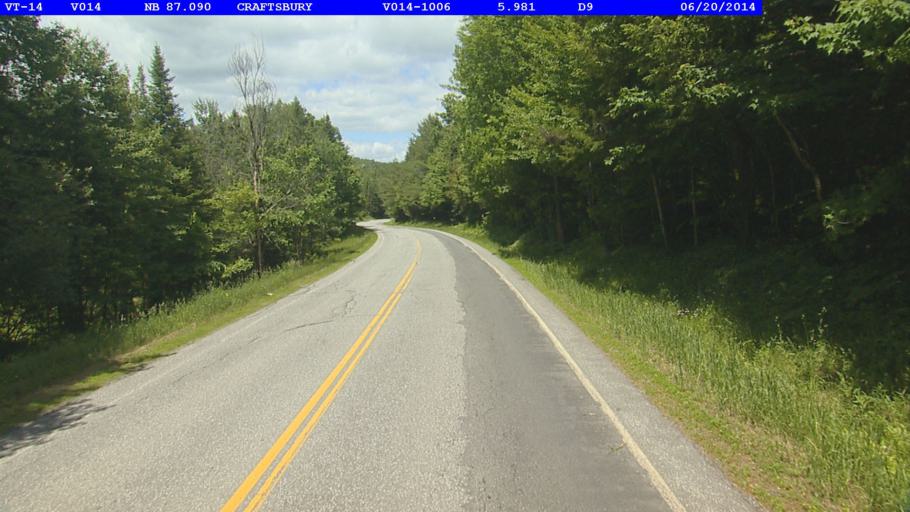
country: US
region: Vermont
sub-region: Caledonia County
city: Hardwick
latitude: 44.6766
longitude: -72.4045
